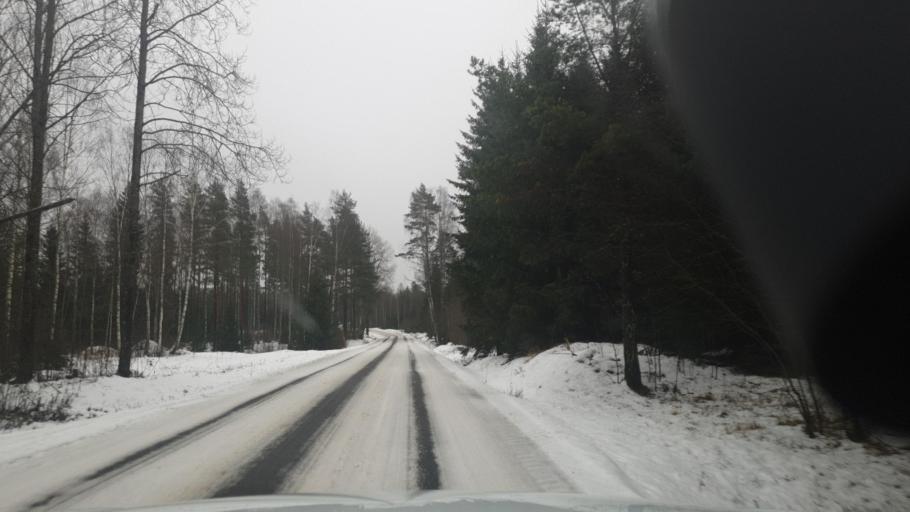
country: SE
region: Vaermland
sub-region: Karlstads Kommun
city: Valberg
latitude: 59.4171
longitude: 13.1223
